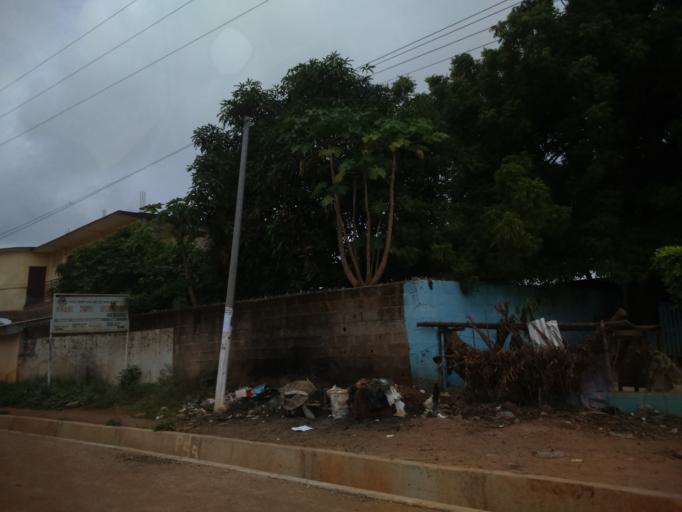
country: CI
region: Moyen-Comoe
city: Abengourou
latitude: 6.7261
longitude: -3.5034
